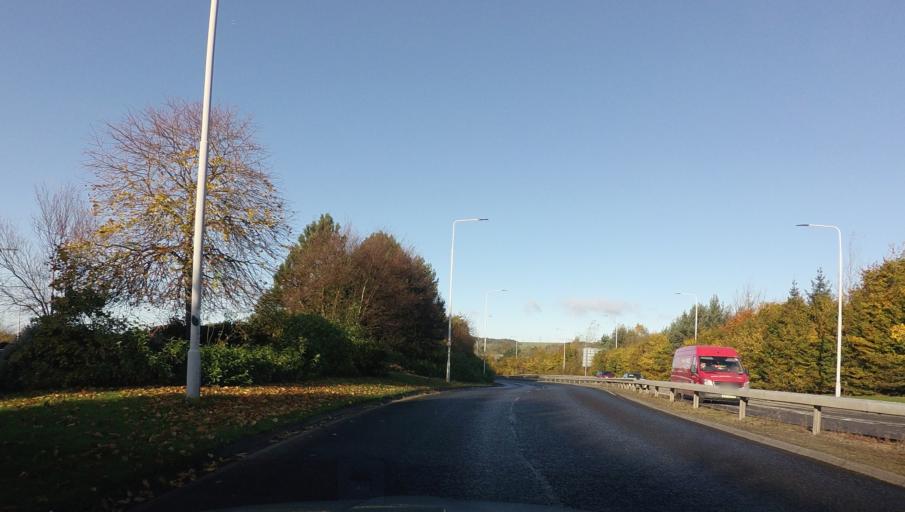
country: GB
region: Scotland
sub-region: Fife
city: Crossgates
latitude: 56.0816
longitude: -3.3995
